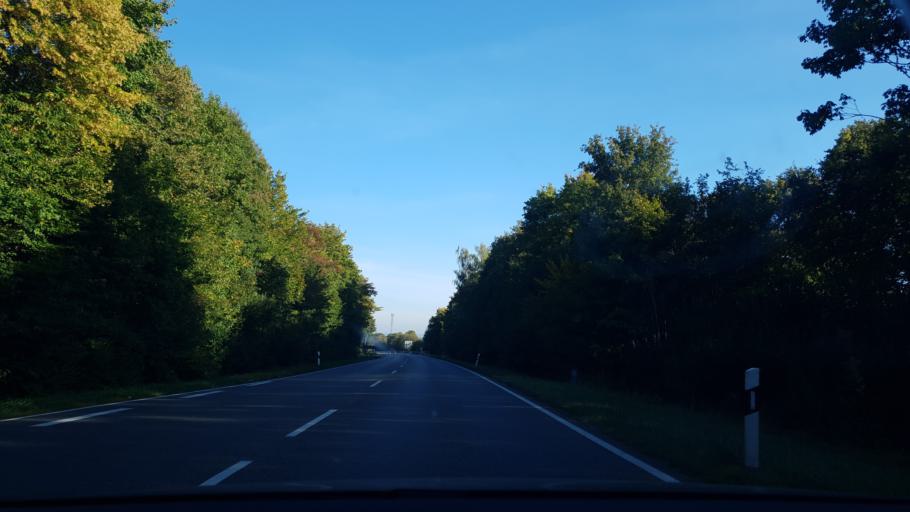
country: DE
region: Hesse
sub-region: Regierungsbezirk Giessen
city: Langgons
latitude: 50.4816
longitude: 8.6571
